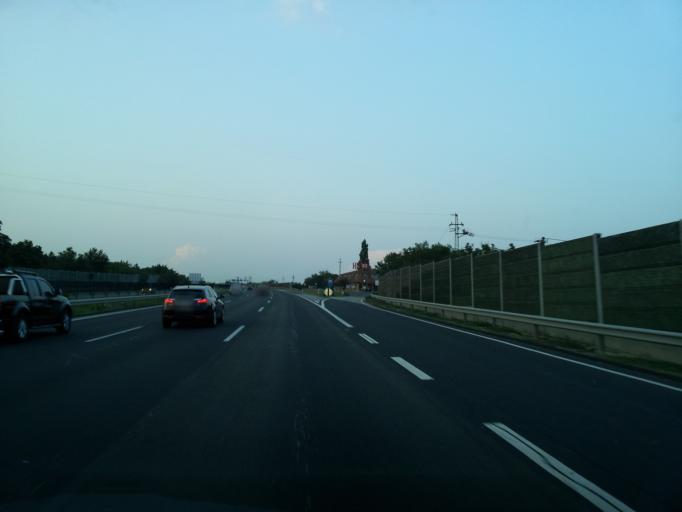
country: HU
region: Pest
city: Tarnok
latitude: 47.3998
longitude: 18.8687
